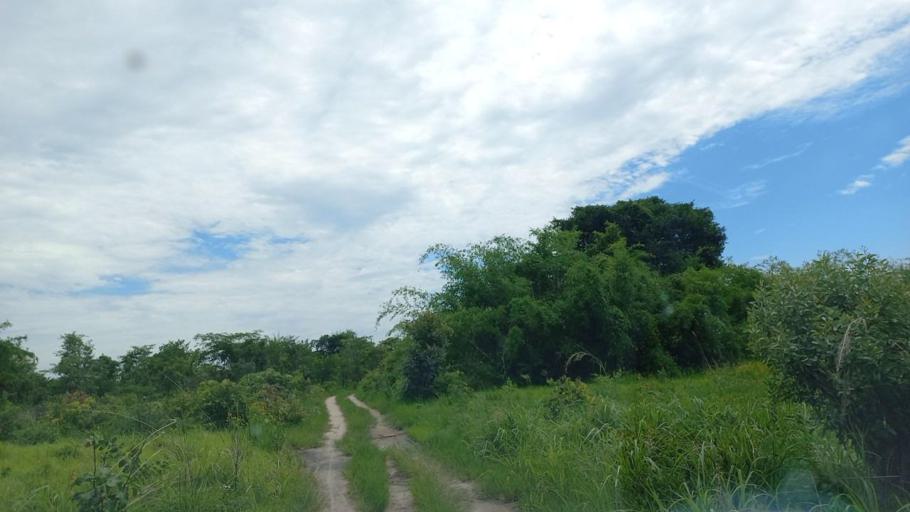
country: ZM
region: Copperbelt
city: Kitwe
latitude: -12.7896
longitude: 28.3942
